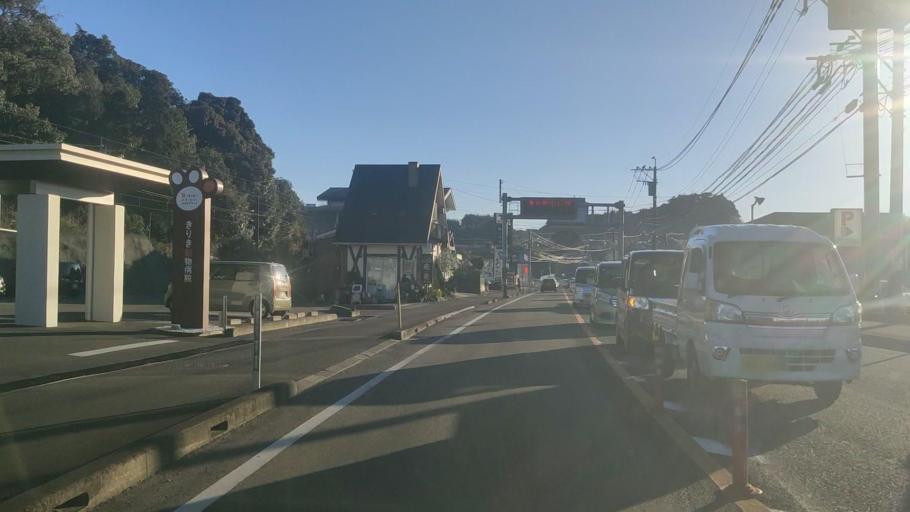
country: JP
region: Miyazaki
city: Miyazaki-shi
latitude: 31.8698
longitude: 131.3929
